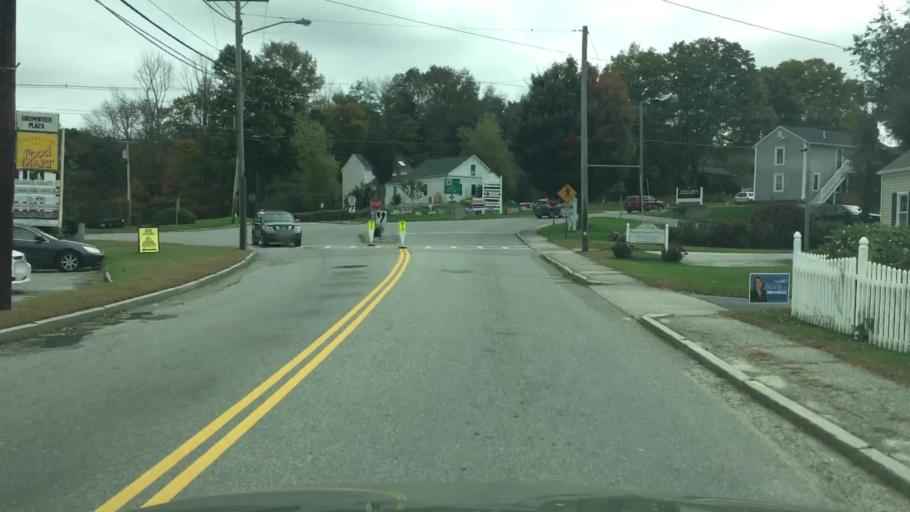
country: US
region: Massachusetts
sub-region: Worcester County
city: Charlton
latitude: 42.1370
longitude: -71.9707
